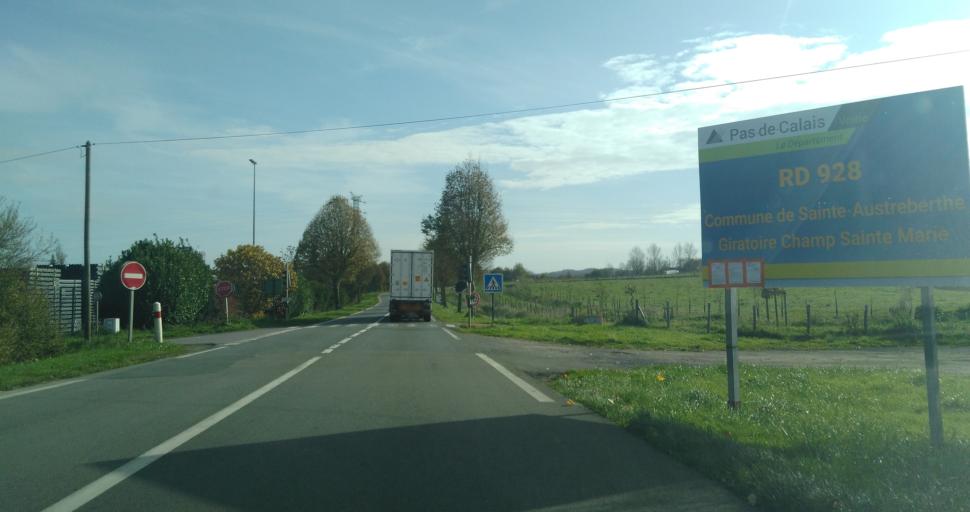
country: FR
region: Nord-Pas-de-Calais
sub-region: Departement du Pas-de-Calais
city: Hesdin
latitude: 50.3667
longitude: 2.0330
